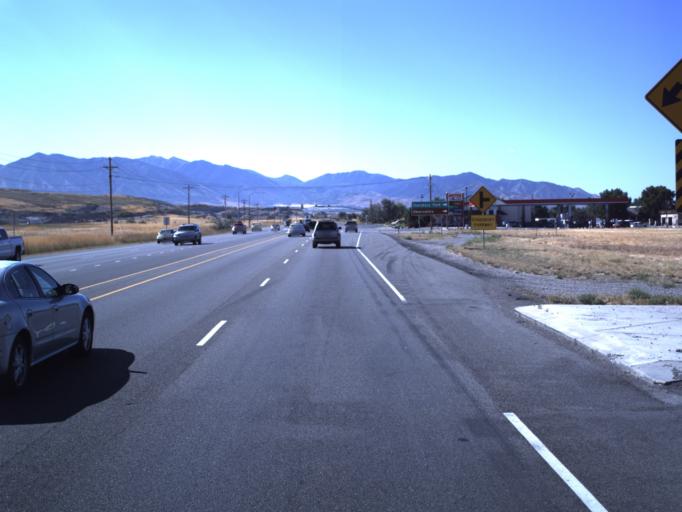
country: US
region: Utah
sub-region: Tooele County
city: Stansbury park
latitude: 40.6497
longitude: -112.2888
